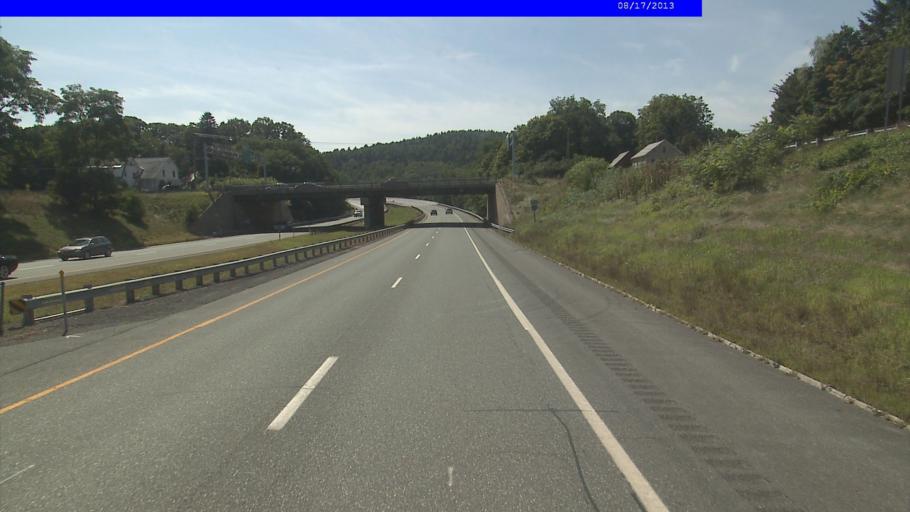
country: US
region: Vermont
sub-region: Windham County
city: Brattleboro
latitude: 42.8515
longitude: -72.5798
